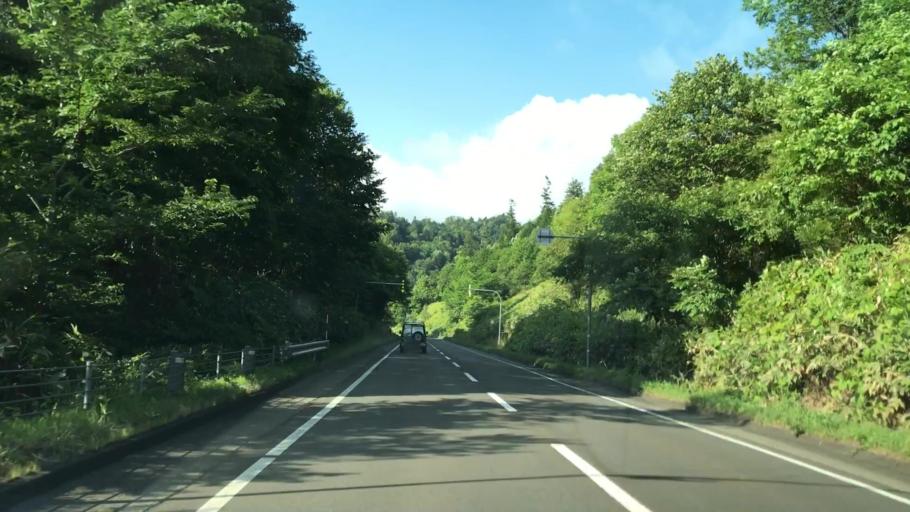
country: JP
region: Hokkaido
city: Iwamizawa
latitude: 42.9008
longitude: 142.1268
